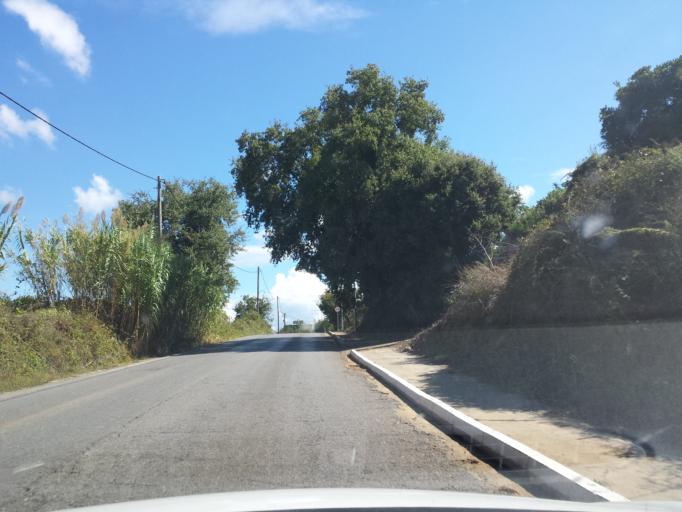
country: GR
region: Peloponnese
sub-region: Nomos Messinias
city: Vlakhopoulon
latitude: 36.9624
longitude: 21.7986
